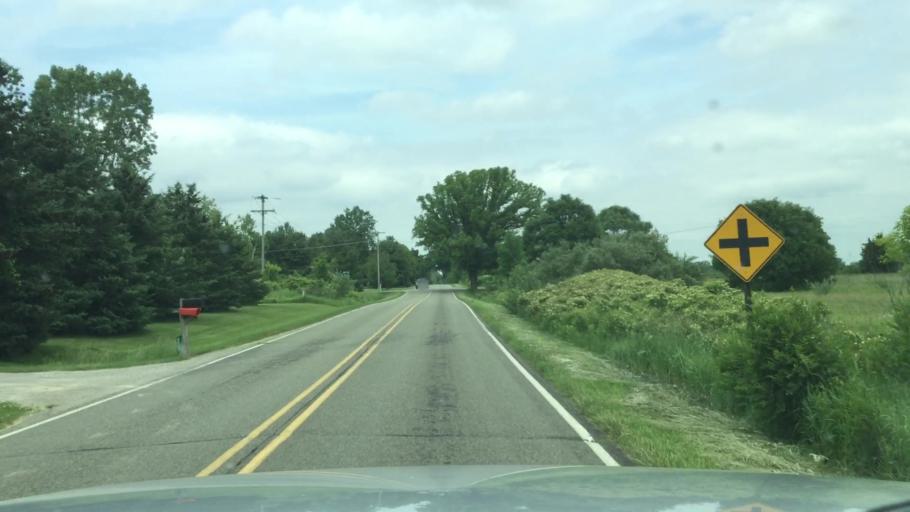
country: US
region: Michigan
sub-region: Shiawassee County
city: Durand
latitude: 42.9391
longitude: -83.9590
